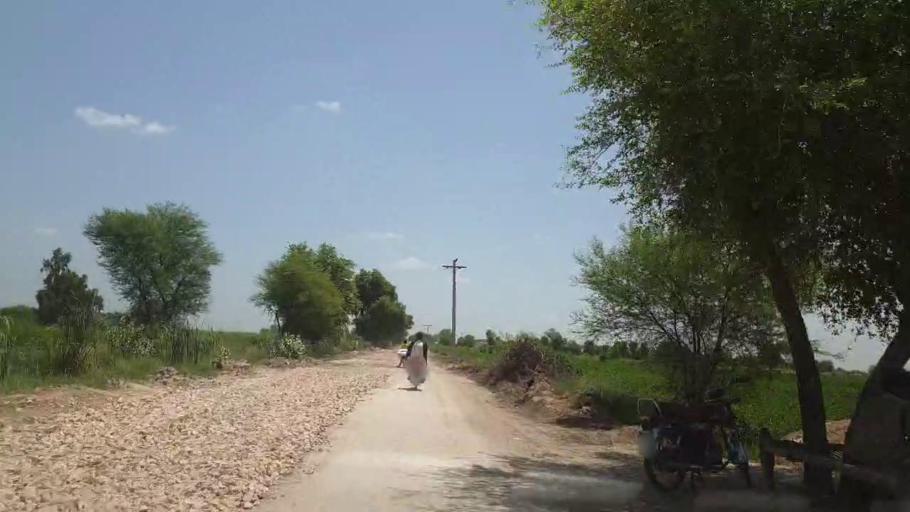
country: PK
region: Sindh
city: Pano Aqil
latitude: 27.6656
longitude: 69.1931
